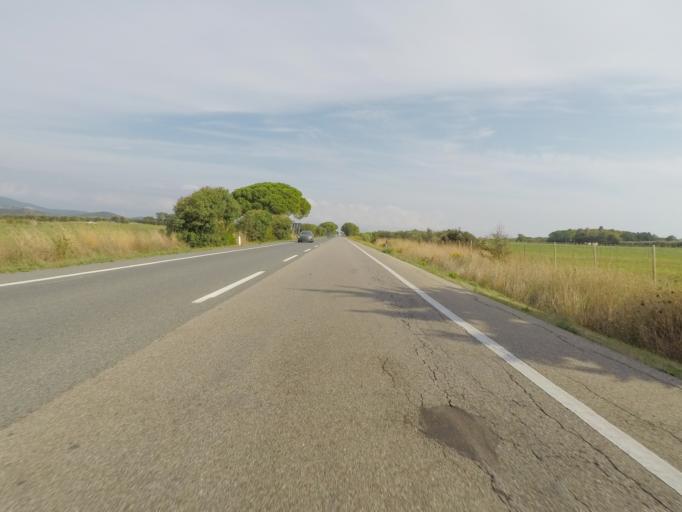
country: IT
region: Tuscany
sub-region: Provincia di Grosseto
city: Capalbio
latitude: 42.4151
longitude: 11.3588
